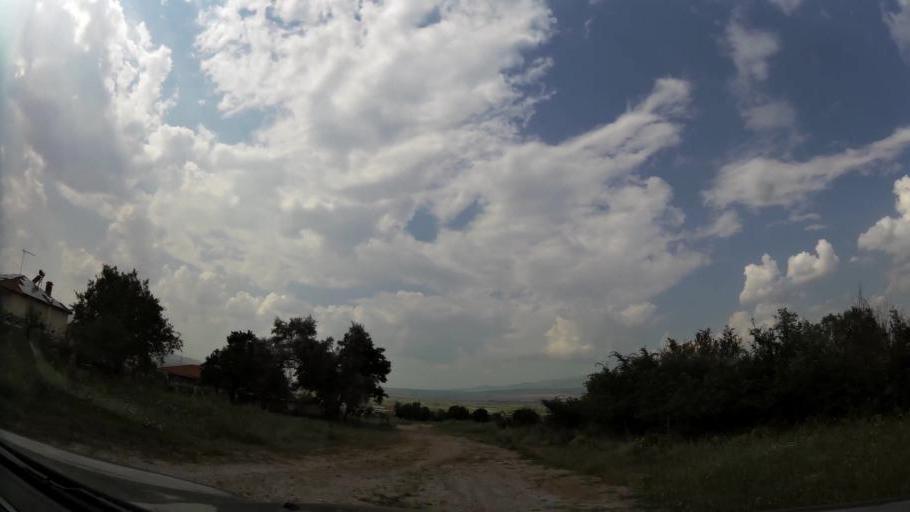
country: GR
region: West Macedonia
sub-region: Nomos Kozanis
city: Koila
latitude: 40.3481
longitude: 21.8437
